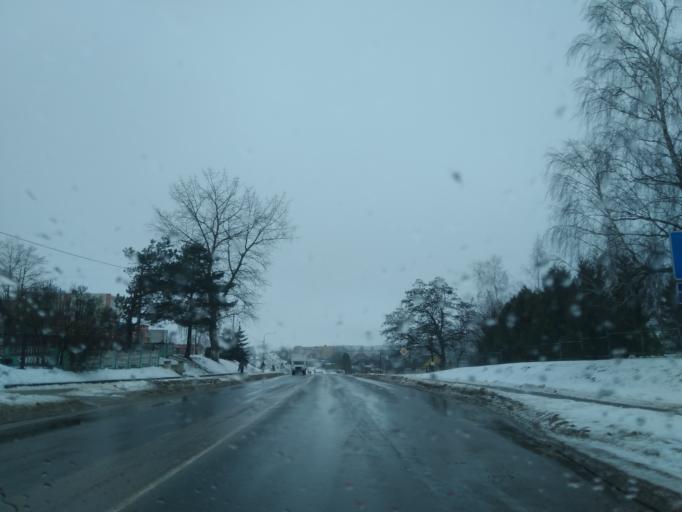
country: BY
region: Minsk
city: Nyasvizh
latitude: 53.2322
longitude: 26.6540
